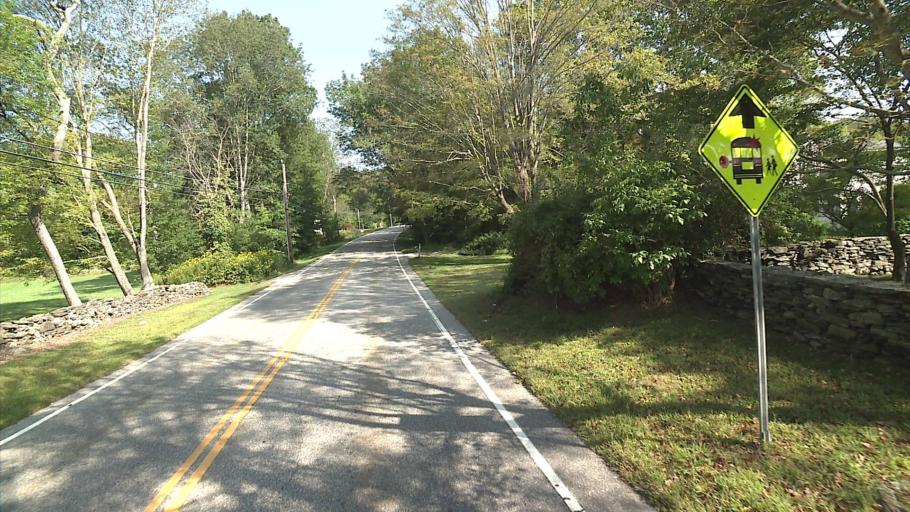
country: US
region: Connecticut
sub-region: Windham County
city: Plainfield Village
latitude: 41.6637
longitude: -71.9734
